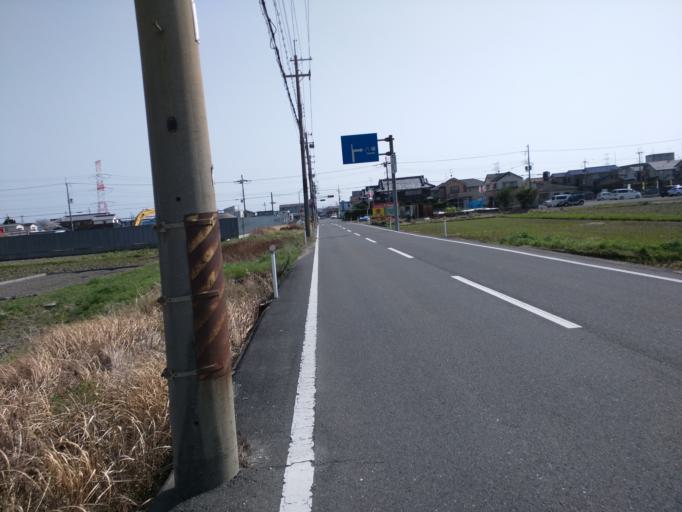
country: JP
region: Kyoto
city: Tanabe
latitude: 34.7639
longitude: 135.7973
